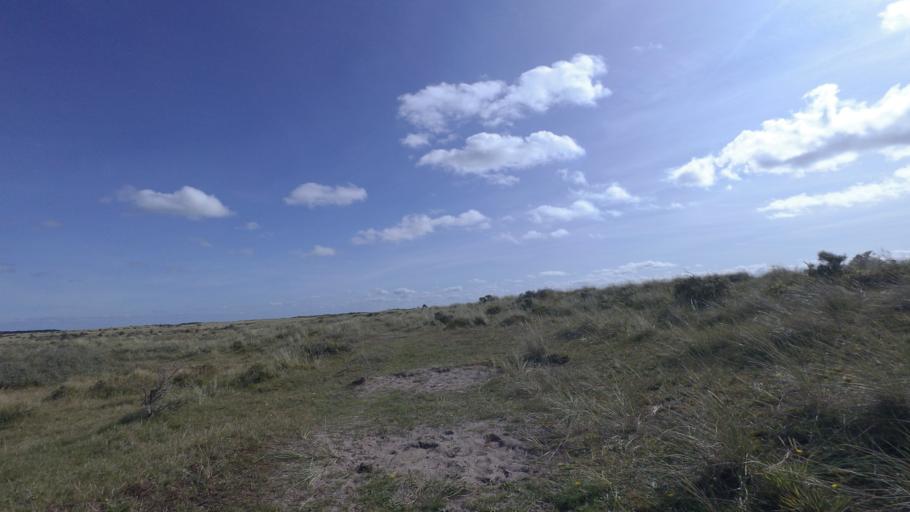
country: NL
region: Friesland
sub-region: Gemeente Ameland
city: Nes
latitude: 53.4508
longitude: 5.7327
